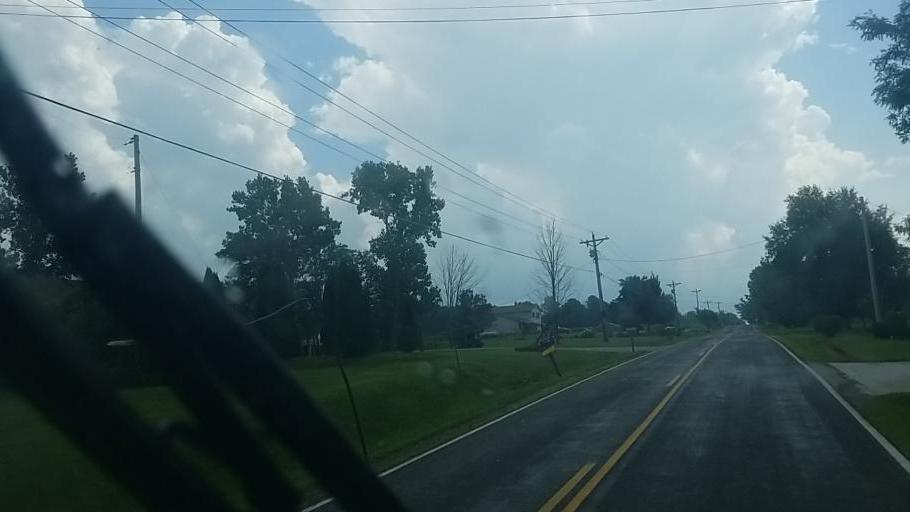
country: US
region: Ohio
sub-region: Lorain County
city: Grafton
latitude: 41.1641
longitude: -82.0036
